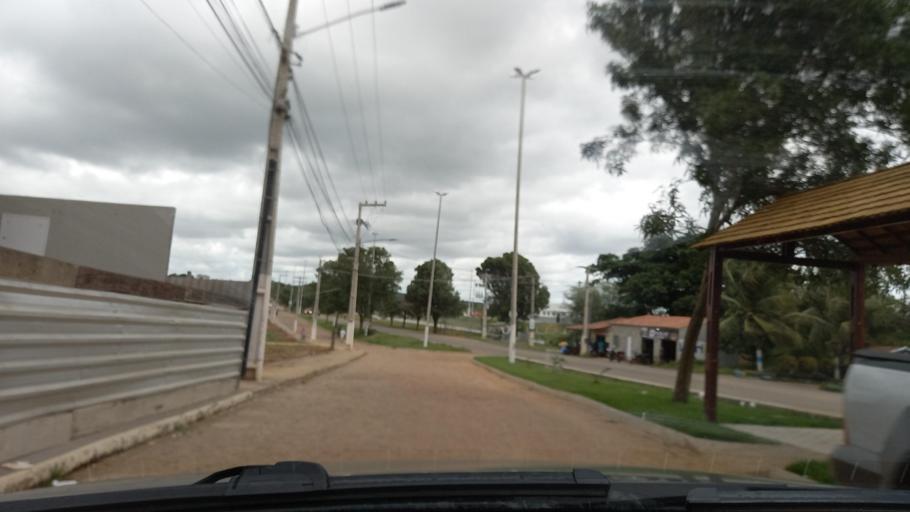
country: BR
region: Sergipe
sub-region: Caninde De Sao Francisco
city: Caninde de Sao Francisco
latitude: -9.6676
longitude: -37.7934
